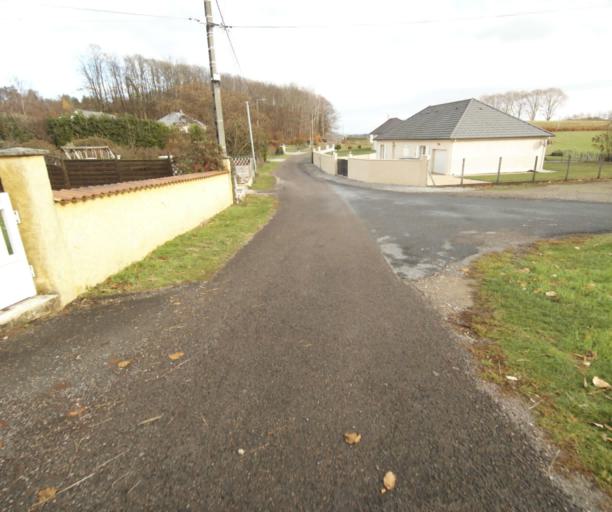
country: FR
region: Limousin
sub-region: Departement de la Correze
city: Saint-Mexant
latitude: 45.2796
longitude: 1.6465
